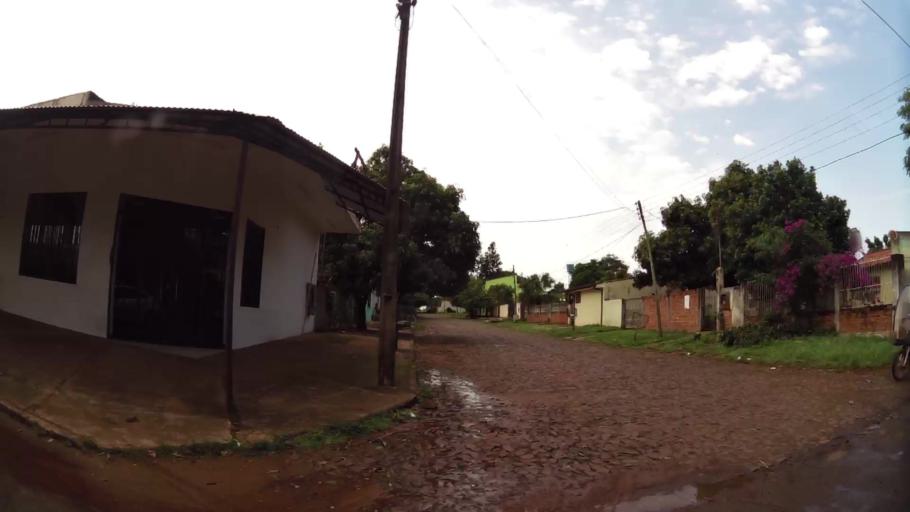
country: PY
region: Alto Parana
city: Ciudad del Este
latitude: -25.5054
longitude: -54.6670
